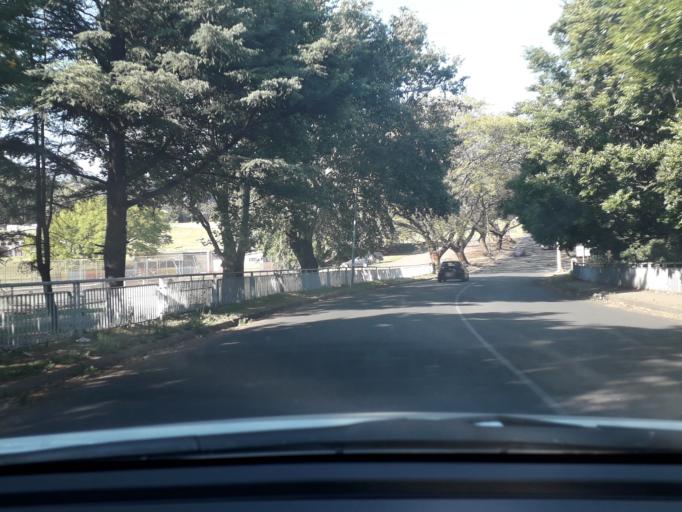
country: ZA
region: Gauteng
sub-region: City of Johannesburg Metropolitan Municipality
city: Johannesburg
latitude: -26.1728
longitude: 28.0151
